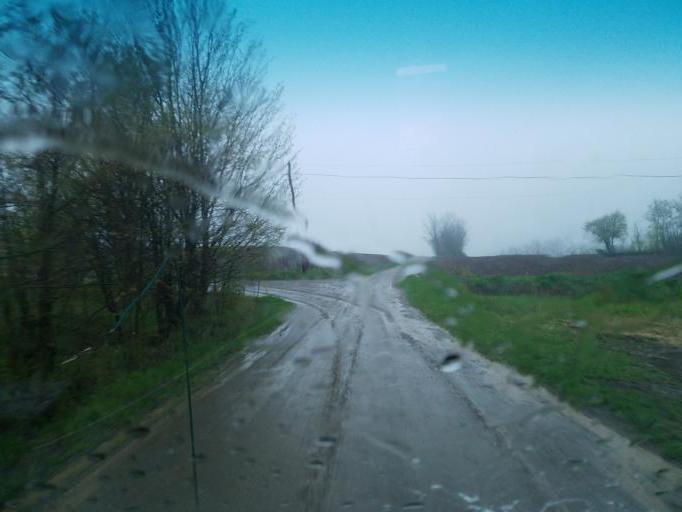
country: US
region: Pennsylvania
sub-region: Tioga County
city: Westfield
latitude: 41.9307
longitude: -77.7223
